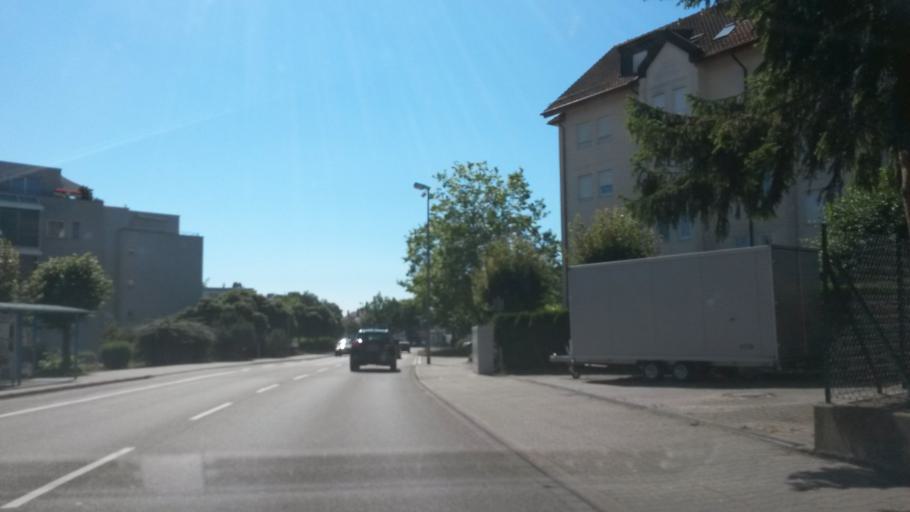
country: DE
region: Baden-Wuerttemberg
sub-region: Karlsruhe Region
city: Ispringen
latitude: 48.8993
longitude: 8.6750
